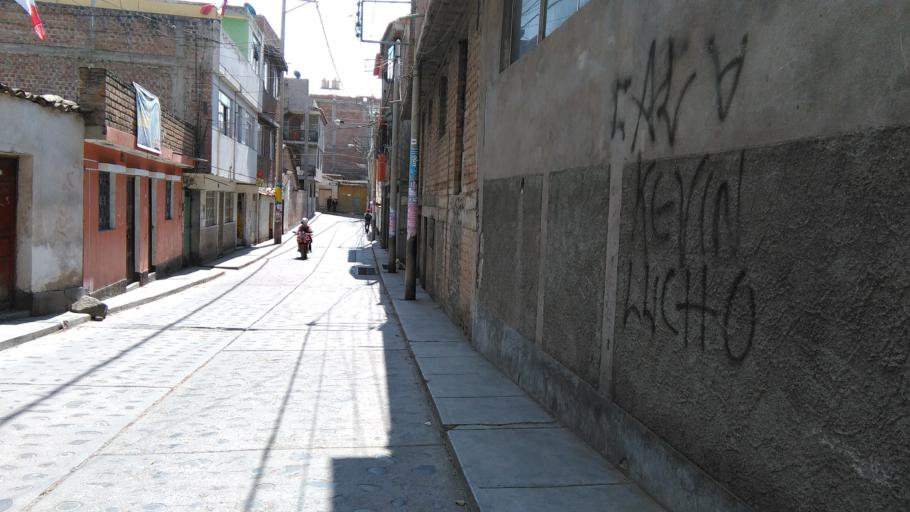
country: PE
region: Ayacucho
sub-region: Provincia de Huamanga
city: Ayacucho
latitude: -13.1605
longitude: -74.2301
